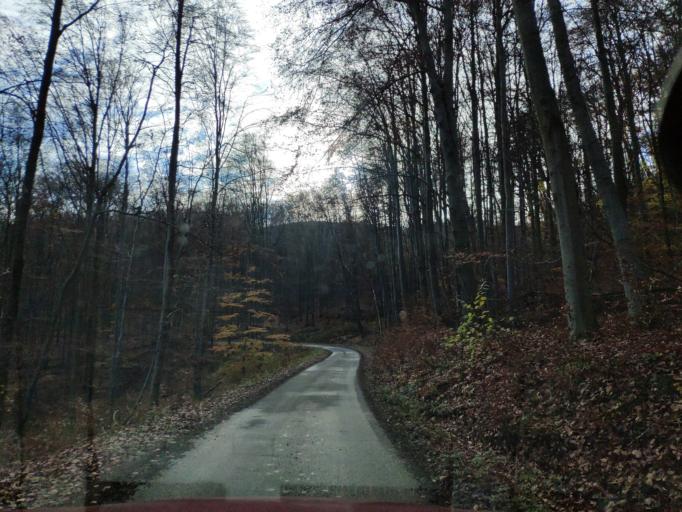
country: HU
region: Borsod-Abauj-Zemplen
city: Gonc
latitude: 48.5826
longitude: 21.4724
